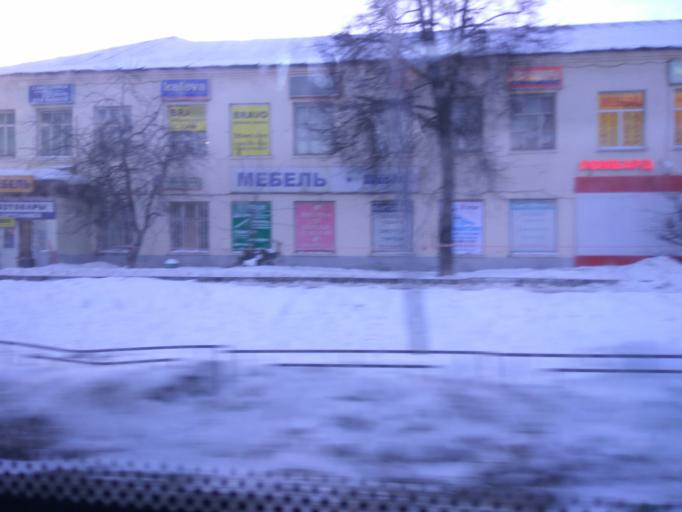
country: RU
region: Moscow
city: Biryulevo
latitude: 55.5913
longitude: 37.6640
